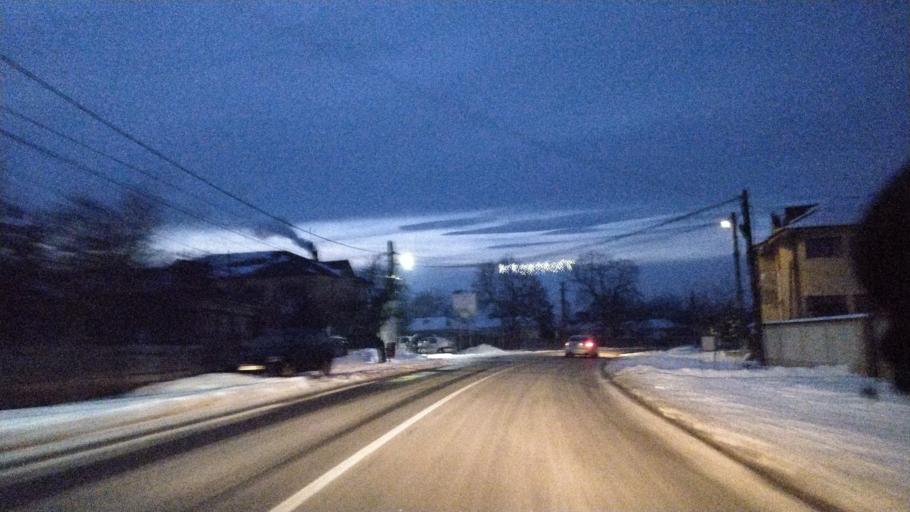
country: RO
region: Vrancea
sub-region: Comuna Rastoaca
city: Rastoaca
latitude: 45.6588
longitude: 27.2833
